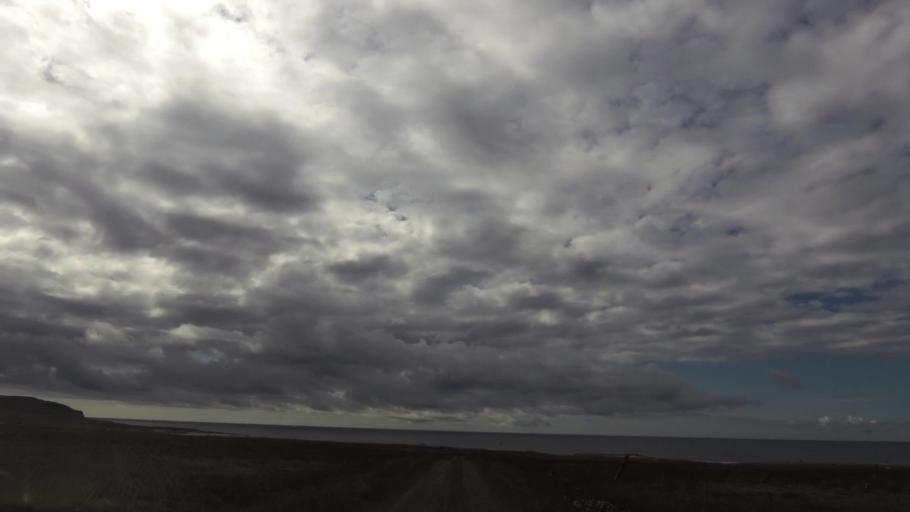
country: IS
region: West
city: Olafsvik
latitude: 65.6142
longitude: -24.3170
